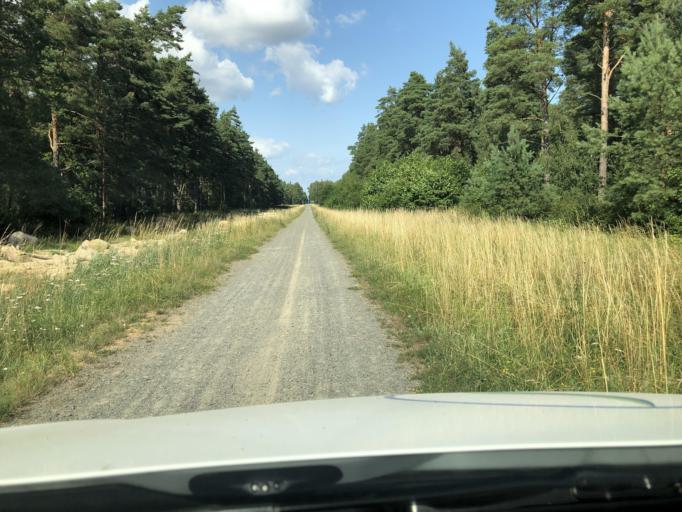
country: SE
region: Skane
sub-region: Kristianstads Kommun
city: Degeberga
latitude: 55.9032
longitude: 14.1050
